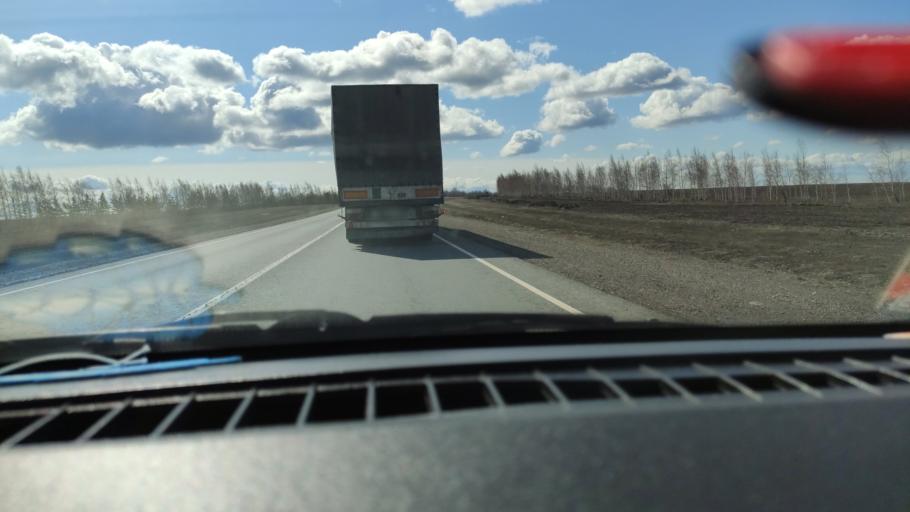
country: RU
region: Samara
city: Syzran'
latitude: 52.9347
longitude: 48.3077
